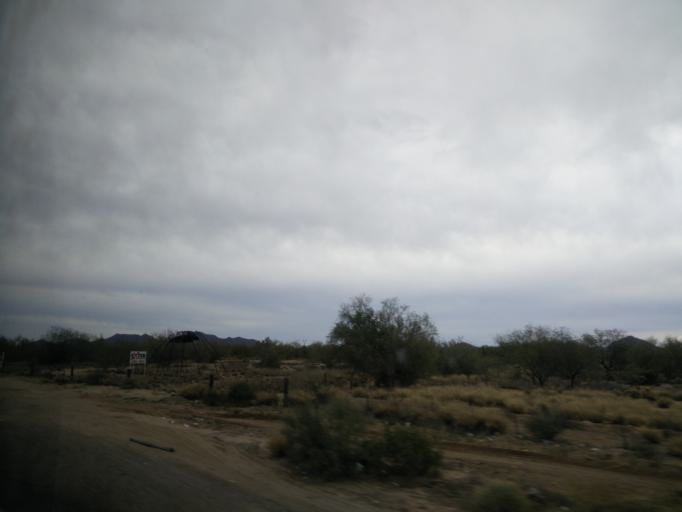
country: MX
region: Sonora
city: Hermosillo
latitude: 28.7333
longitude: -110.9775
